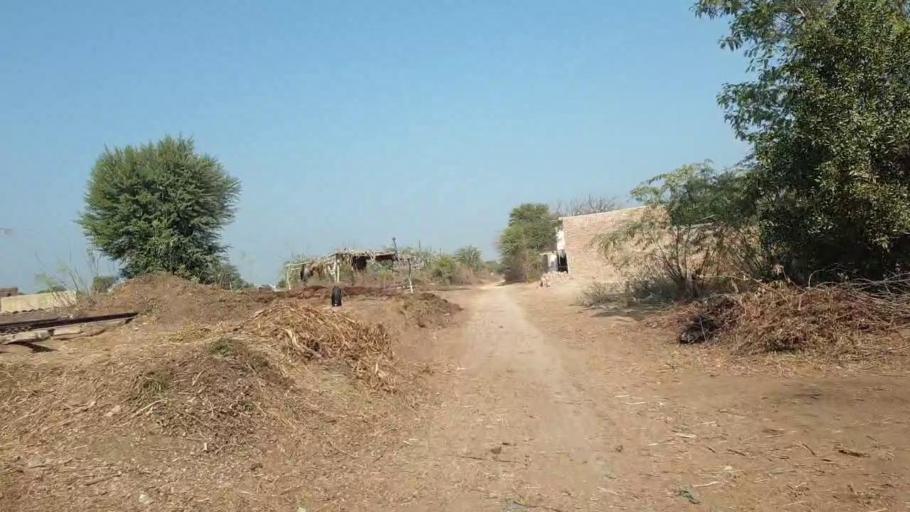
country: PK
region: Sindh
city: Hala
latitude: 25.8874
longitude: 68.4035
